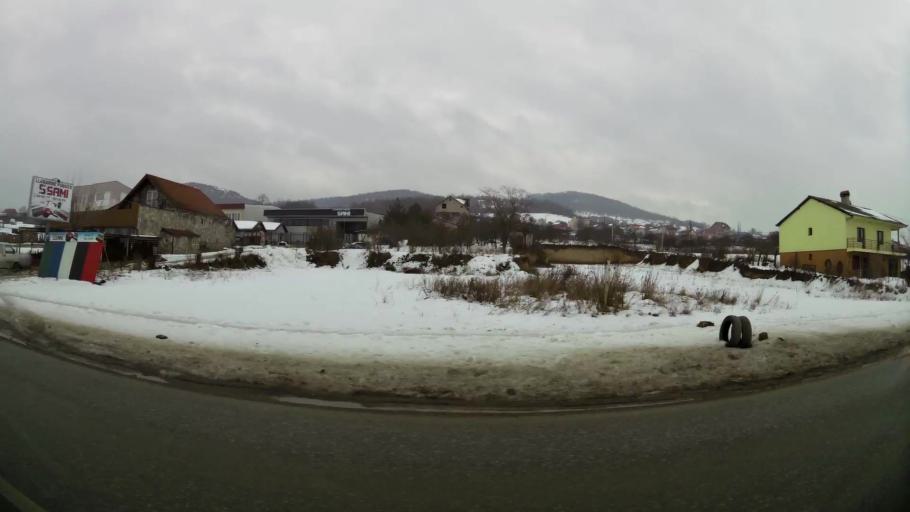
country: XK
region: Pristina
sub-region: Komuna e Prishtines
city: Pristina
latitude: 42.7218
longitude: 21.1466
